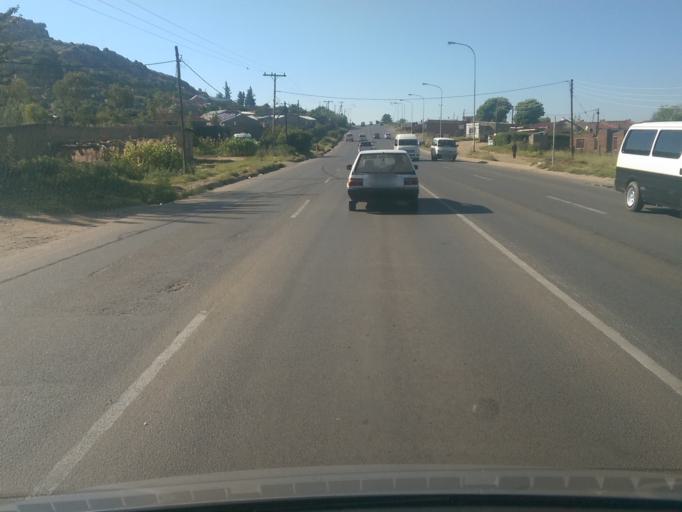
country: LS
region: Maseru
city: Maseru
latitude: -29.3501
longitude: 27.5199
